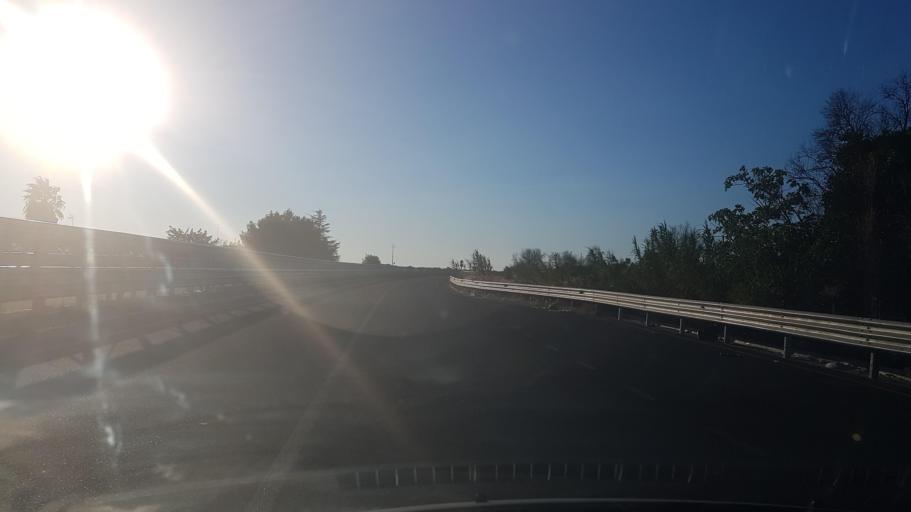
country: IT
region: Apulia
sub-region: Provincia di Lecce
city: Struda
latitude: 40.3173
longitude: 18.2743
